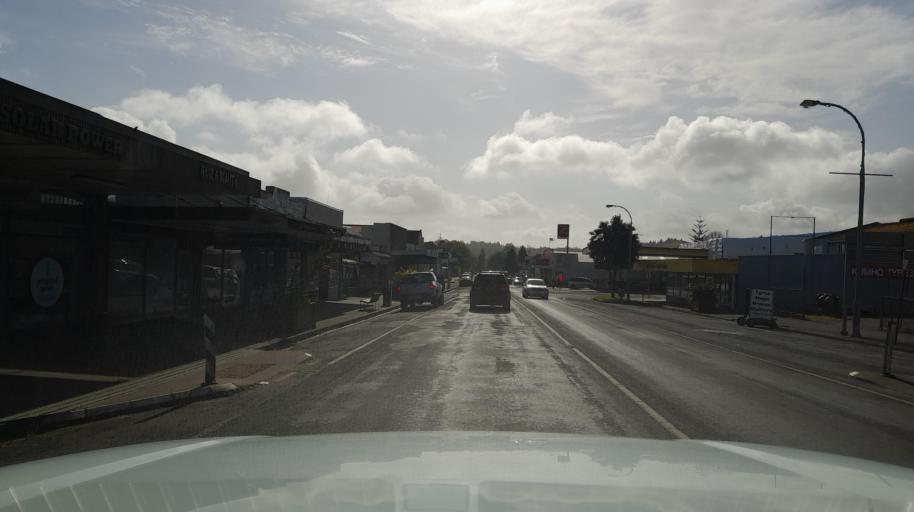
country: NZ
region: Northland
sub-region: Far North District
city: Waimate North
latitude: -35.4065
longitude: 173.8023
